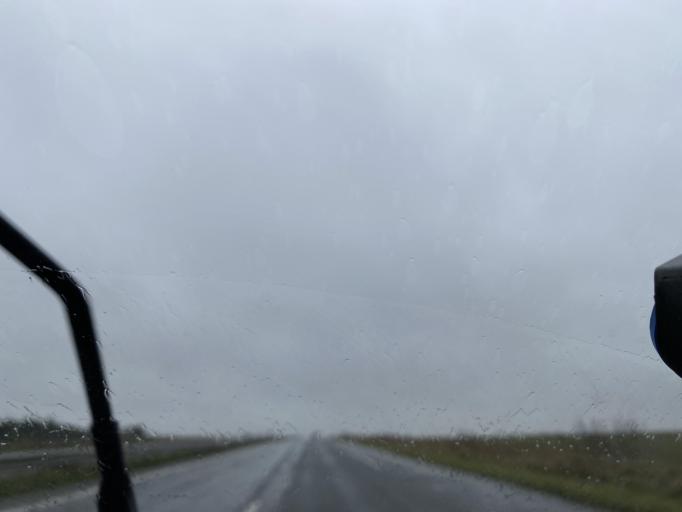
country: FR
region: Centre
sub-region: Departement d'Eure-et-Loir
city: Bailleau-l'Eveque
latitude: 48.5476
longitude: 1.4485
